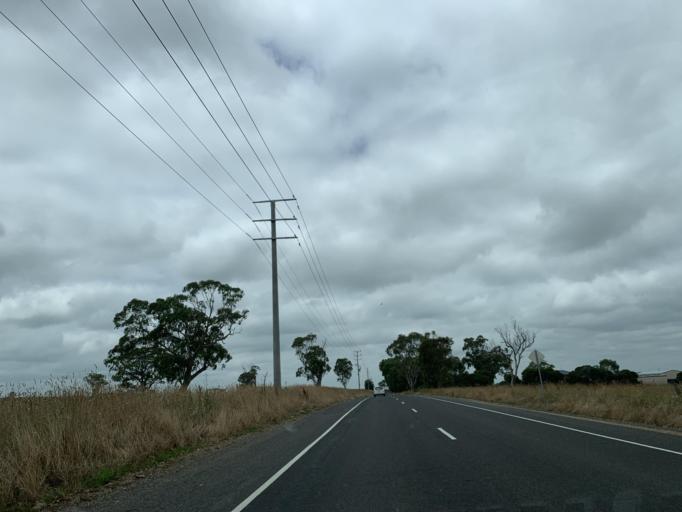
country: AU
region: Victoria
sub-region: Wellington
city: Heyfield
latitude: -37.9857
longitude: 146.8418
